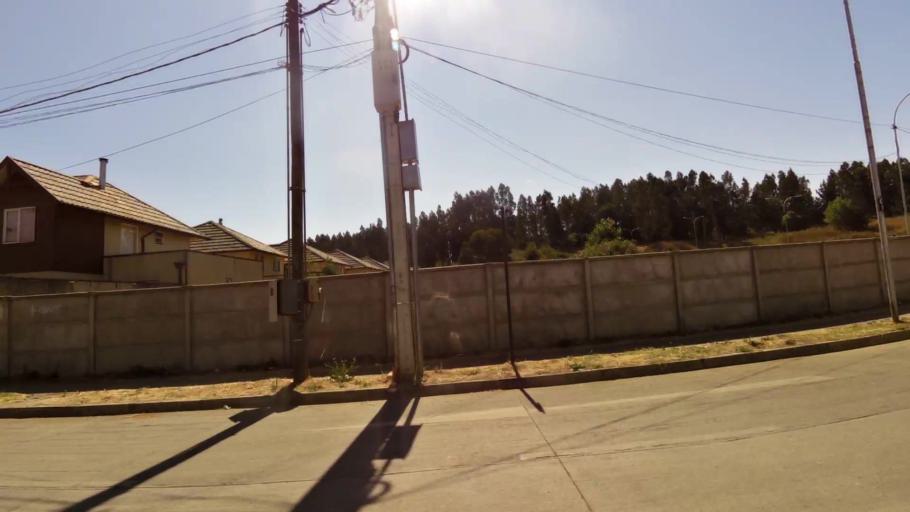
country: CL
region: Biobio
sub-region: Provincia de Concepcion
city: Concepcion
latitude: -36.7883
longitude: -73.0333
